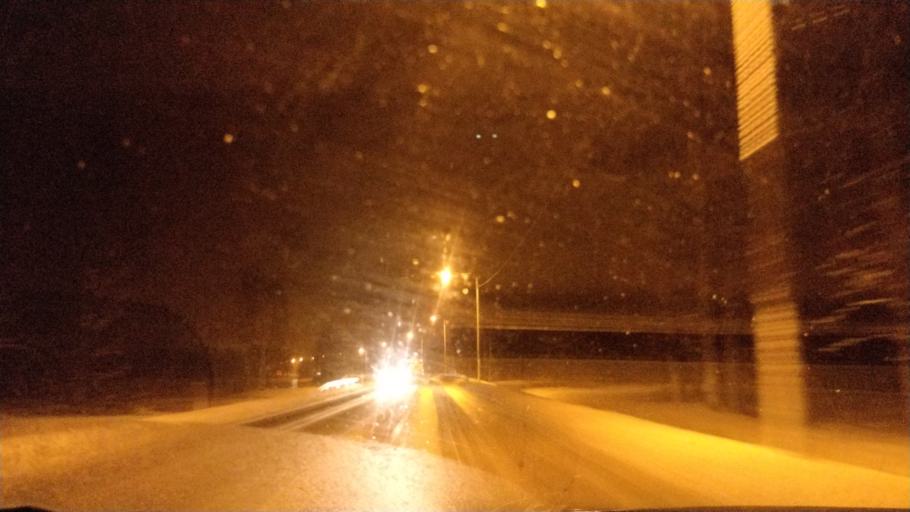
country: FI
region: Lapland
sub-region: Rovaniemi
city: Rovaniemi
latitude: 66.2868
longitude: 25.3437
